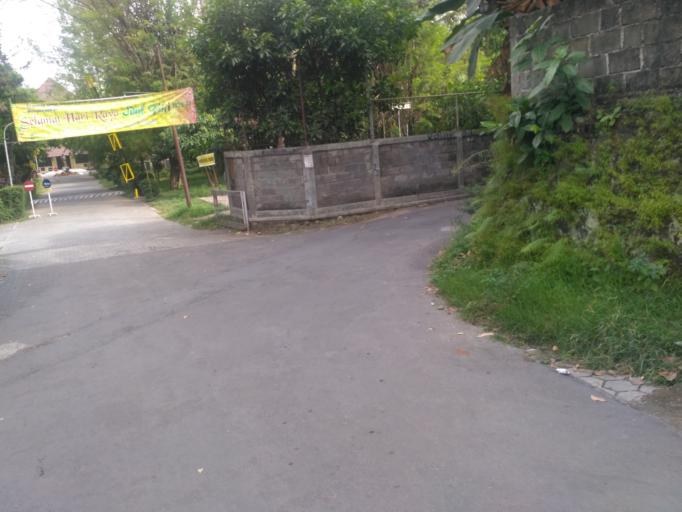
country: ID
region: Daerah Istimewa Yogyakarta
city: Melati
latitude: -7.7545
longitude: 110.3688
